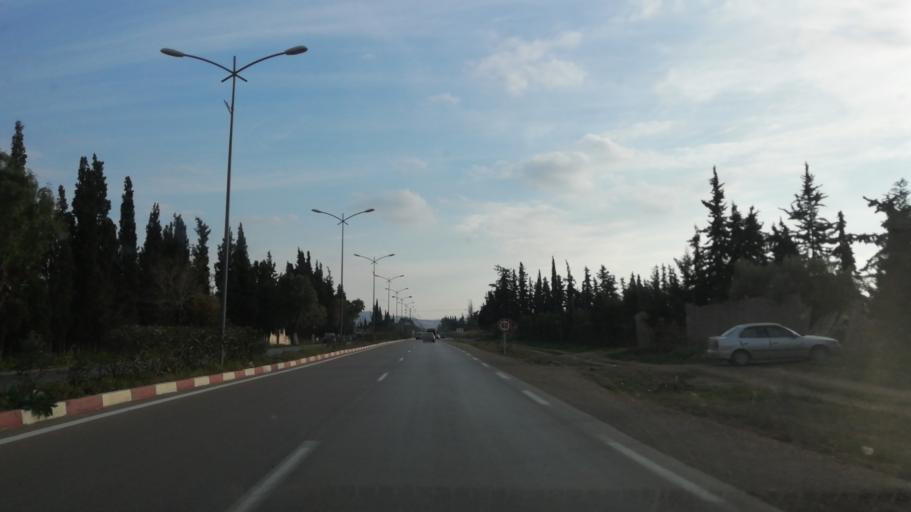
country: DZ
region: Mascara
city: Mascara
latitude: 35.6147
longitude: 0.0625
